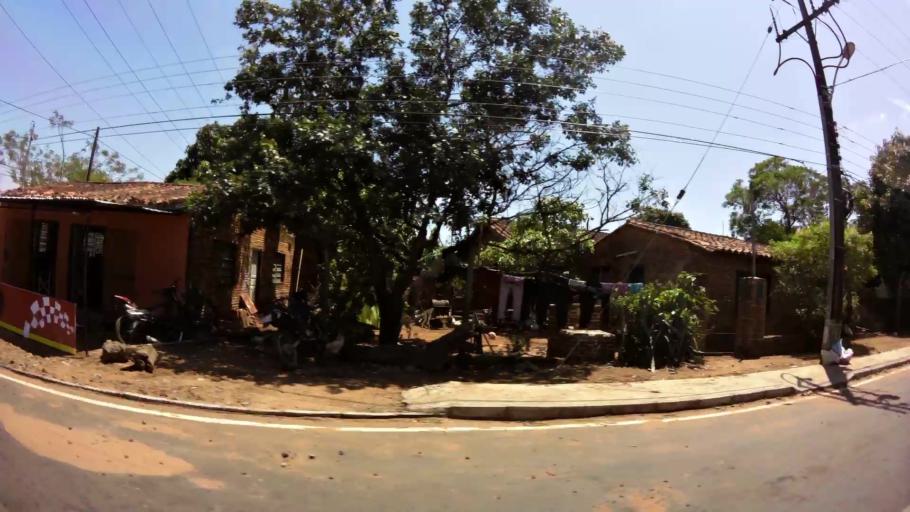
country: PY
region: Central
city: San Antonio
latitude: -25.4143
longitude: -57.5541
